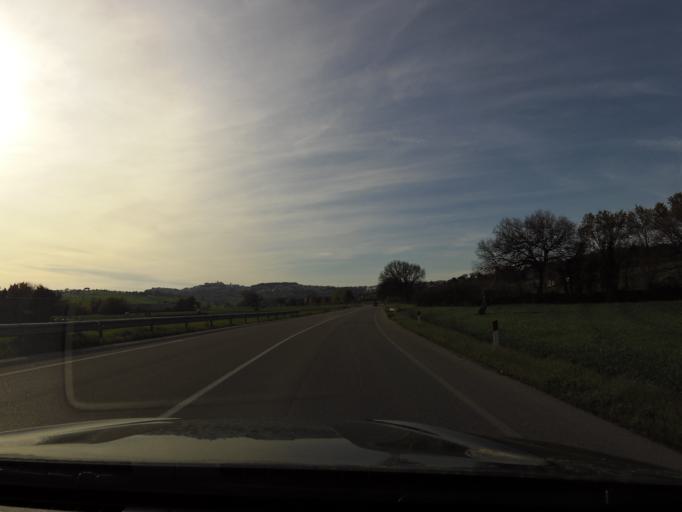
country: IT
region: The Marches
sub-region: Provincia di Ancona
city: Villa Musone
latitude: 43.4565
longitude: 13.5902
